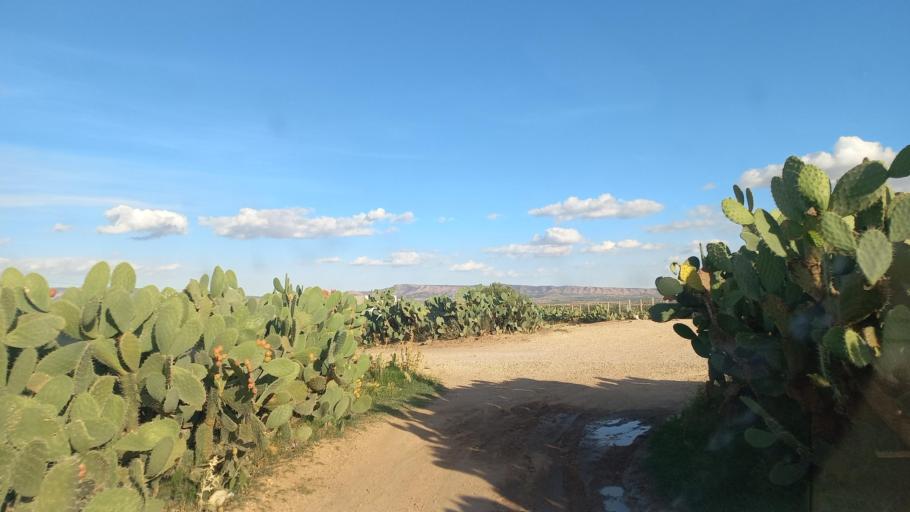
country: TN
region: Al Qasrayn
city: Sbiba
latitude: 35.3797
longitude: 9.0204
